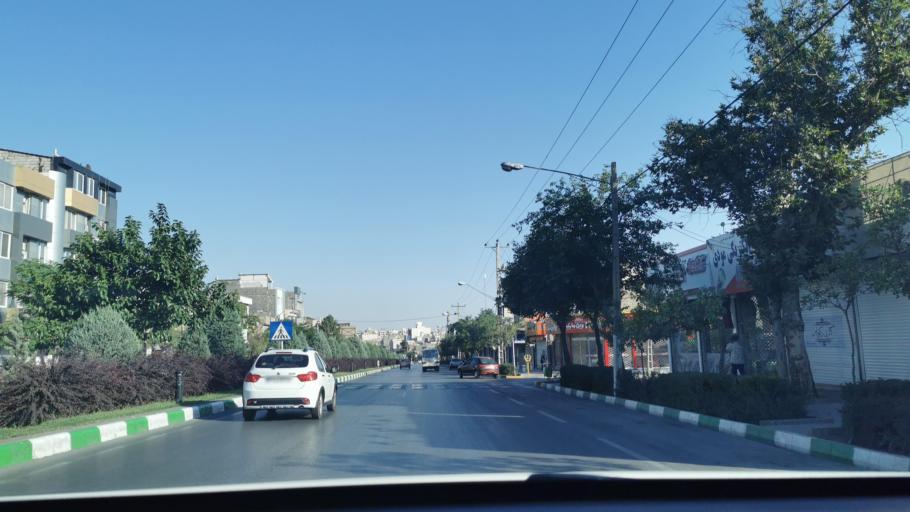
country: IR
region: Razavi Khorasan
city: Mashhad
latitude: 36.3082
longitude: 59.5074
